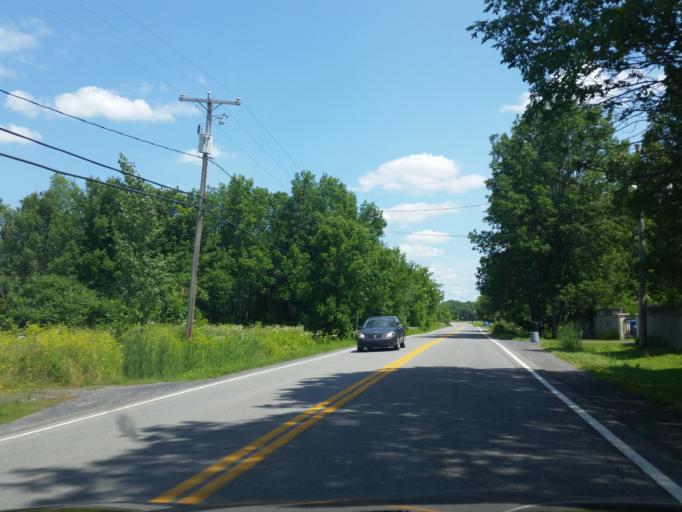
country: CA
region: Quebec
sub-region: Monteregie
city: Richelieu
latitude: 45.4027
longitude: -73.2591
